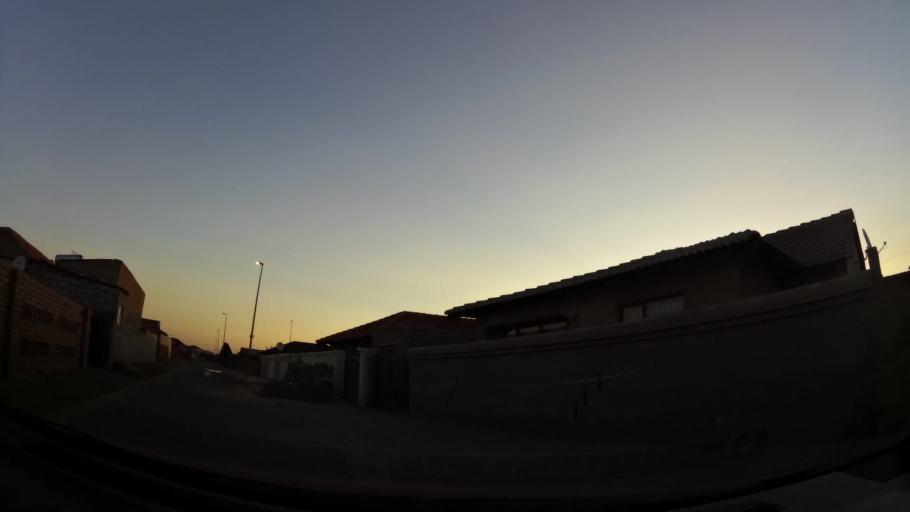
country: ZA
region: Gauteng
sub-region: City of Johannesburg Metropolitan Municipality
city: Soweto
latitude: -26.2256
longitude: 27.8432
